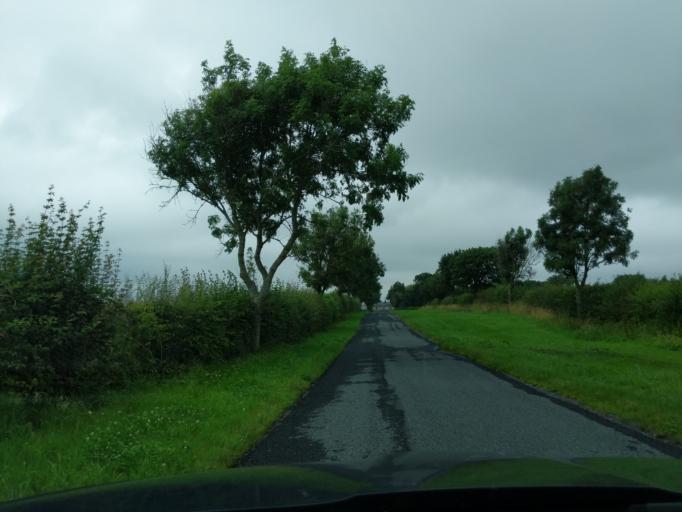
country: GB
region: England
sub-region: Northumberland
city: Ford
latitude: 55.6940
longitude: -2.1343
